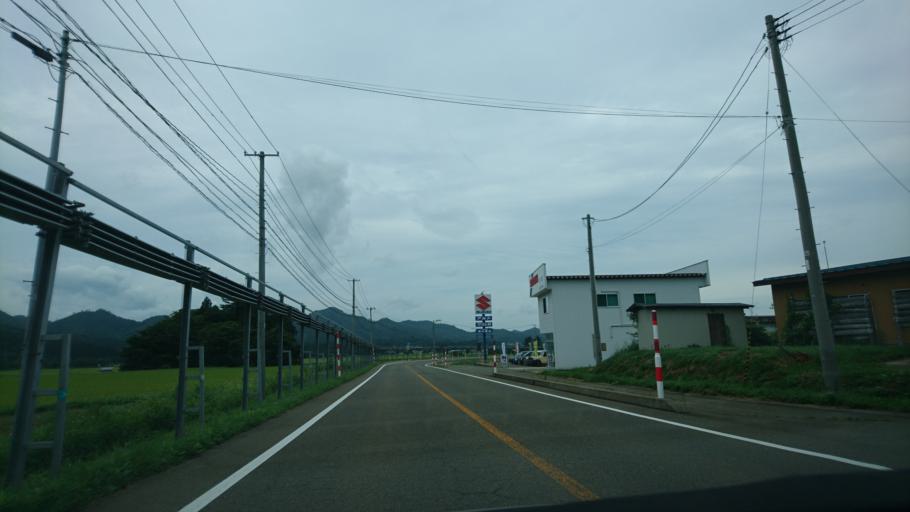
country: JP
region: Akita
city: Yuzawa
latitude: 39.1192
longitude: 140.5797
